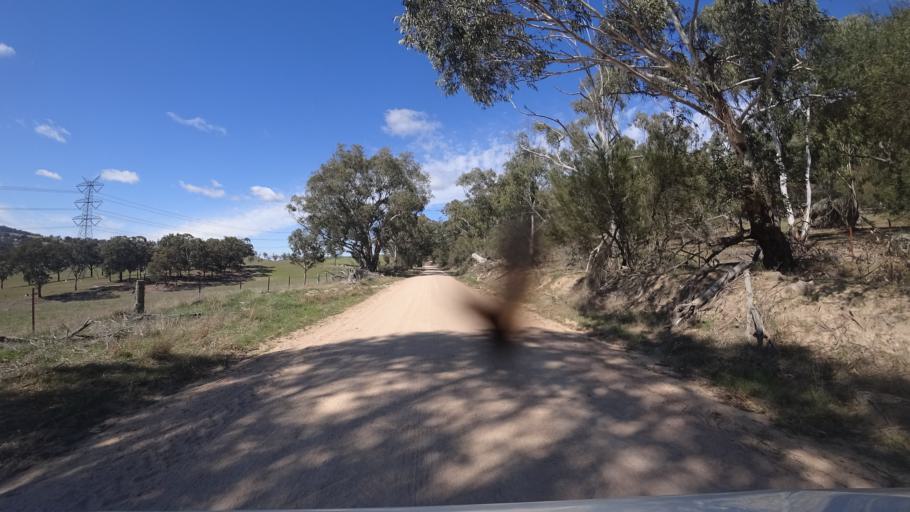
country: AU
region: New South Wales
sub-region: Lithgow
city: Portland
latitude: -33.5338
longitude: 149.9337
